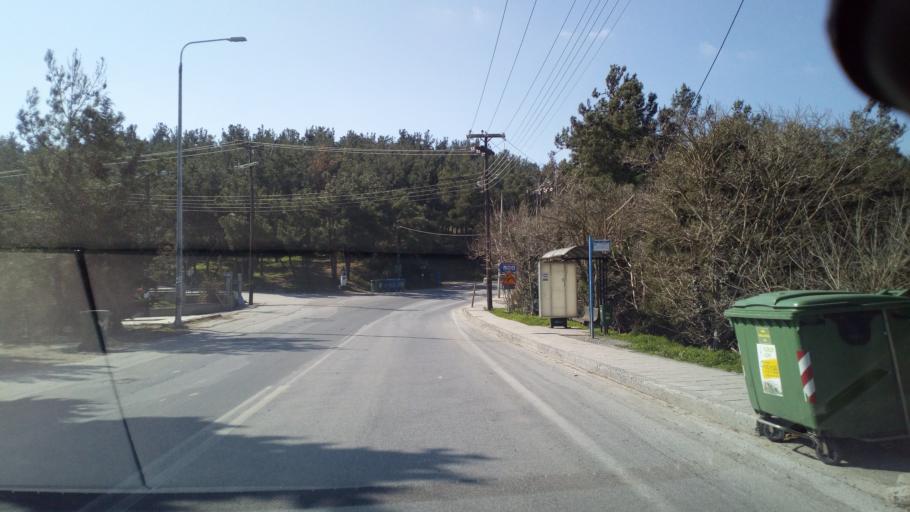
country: GR
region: Central Macedonia
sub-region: Nomos Thessalonikis
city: Panorama
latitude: 40.5936
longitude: 23.0454
